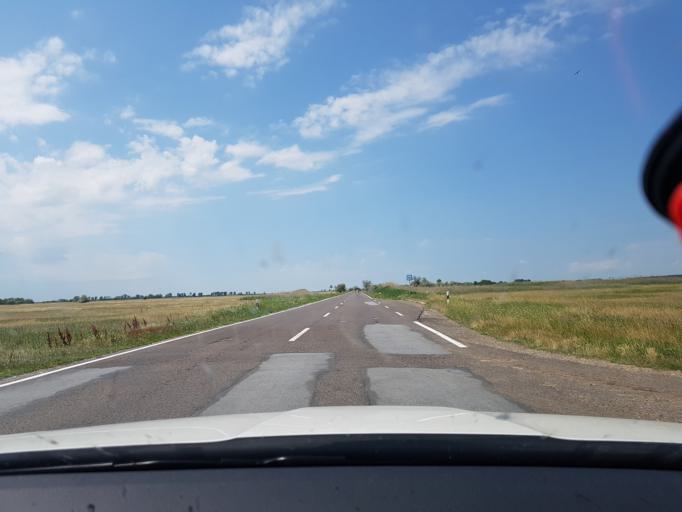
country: HU
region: Hajdu-Bihar
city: Egyek
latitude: 47.5461
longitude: 20.9019
